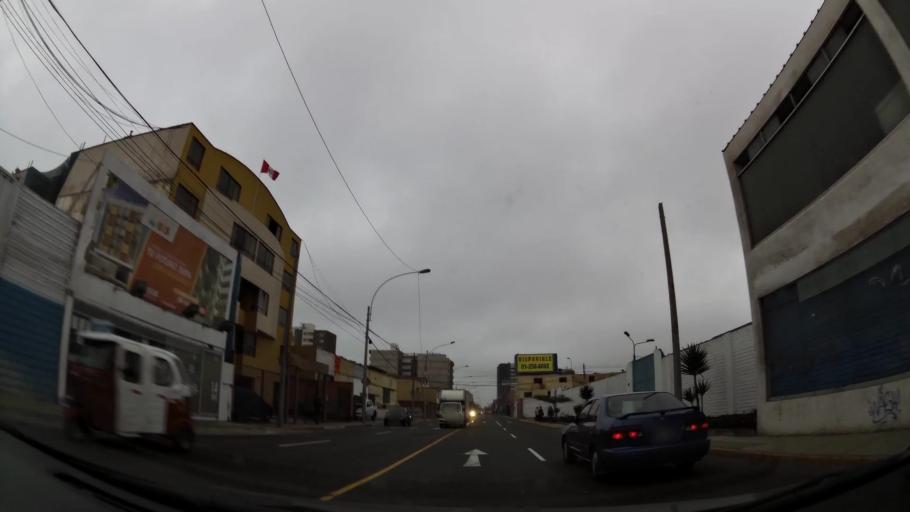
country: PE
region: Callao
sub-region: Callao
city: Callao
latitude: -12.0860
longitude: -77.0925
